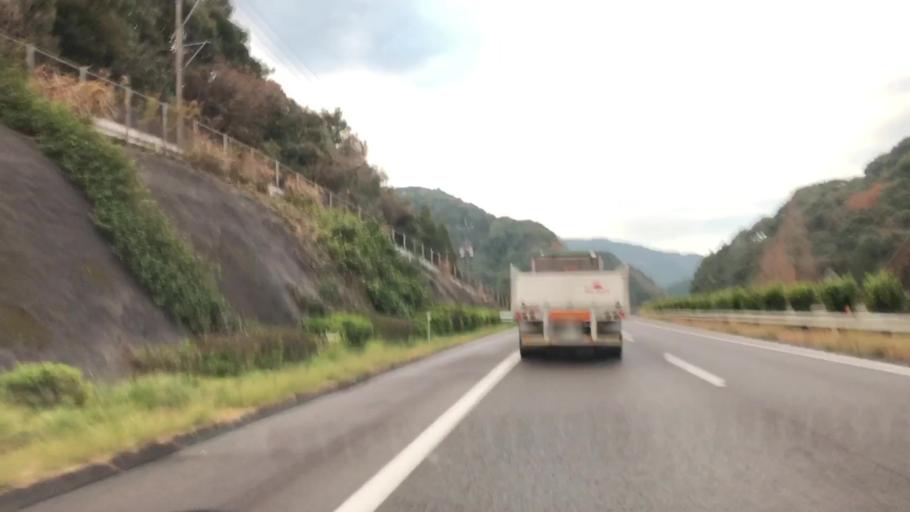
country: JP
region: Saga Prefecture
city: Takeocho-takeo
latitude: 33.1655
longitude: 130.0334
